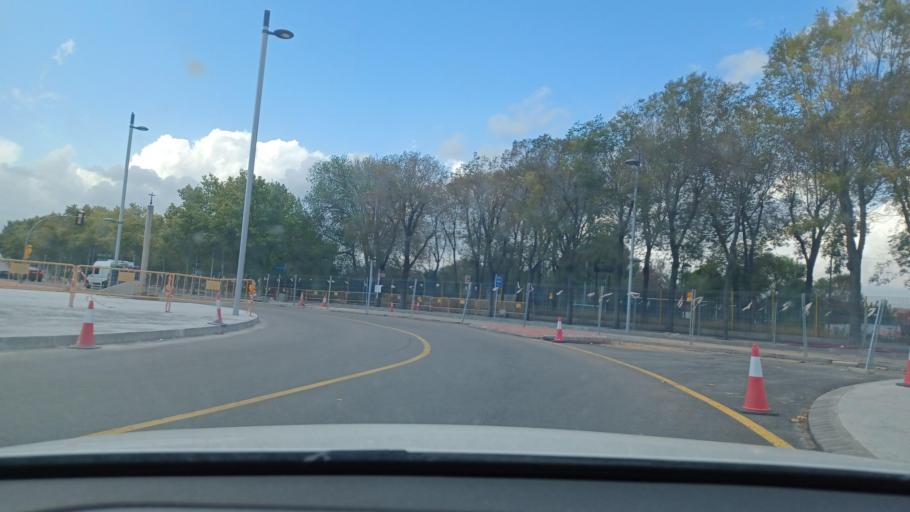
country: ES
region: Catalonia
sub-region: Provincia de Tarragona
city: Tarragona
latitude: 41.1156
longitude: 1.2256
